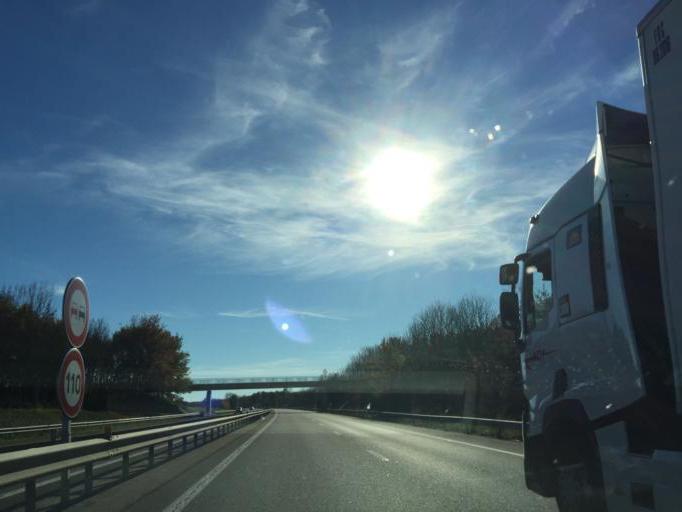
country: FR
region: Rhone-Alpes
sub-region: Departement de la Loire
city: Feurs
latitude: 45.6995
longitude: 4.1601
